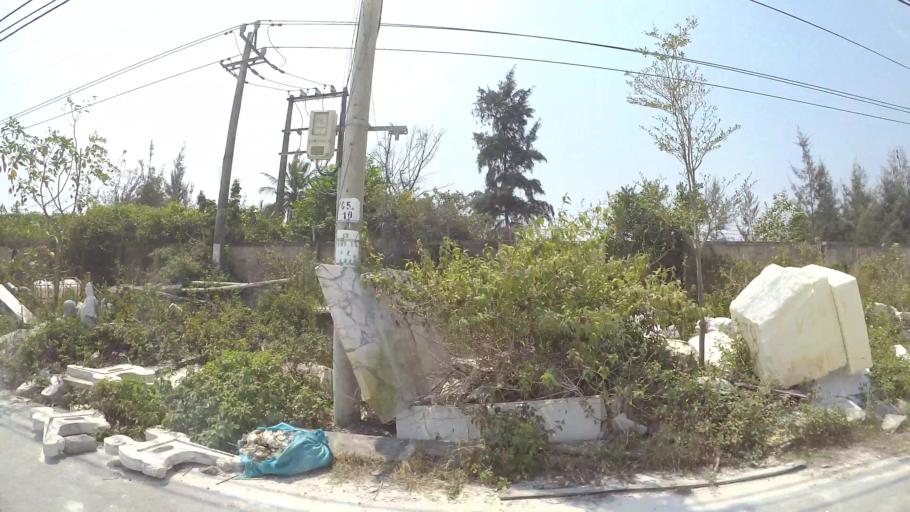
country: VN
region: Da Nang
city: Ngu Hanh Son
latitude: 15.9903
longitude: 108.2536
